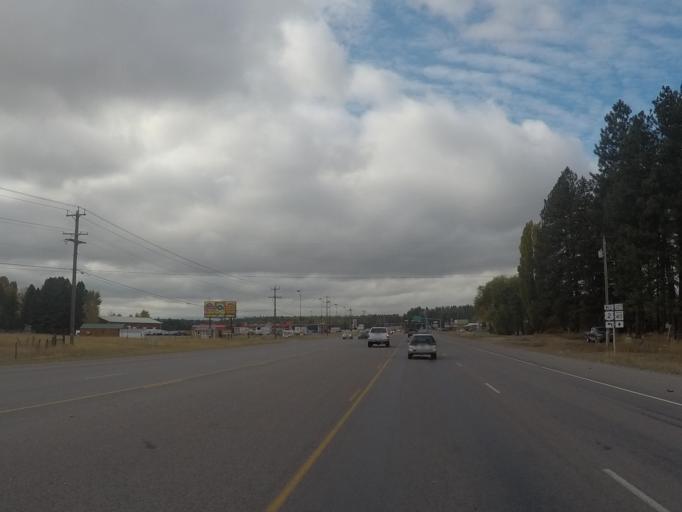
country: US
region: Montana
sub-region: Flathead County
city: Columbia Falls
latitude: 48.3707
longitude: -114.2347
